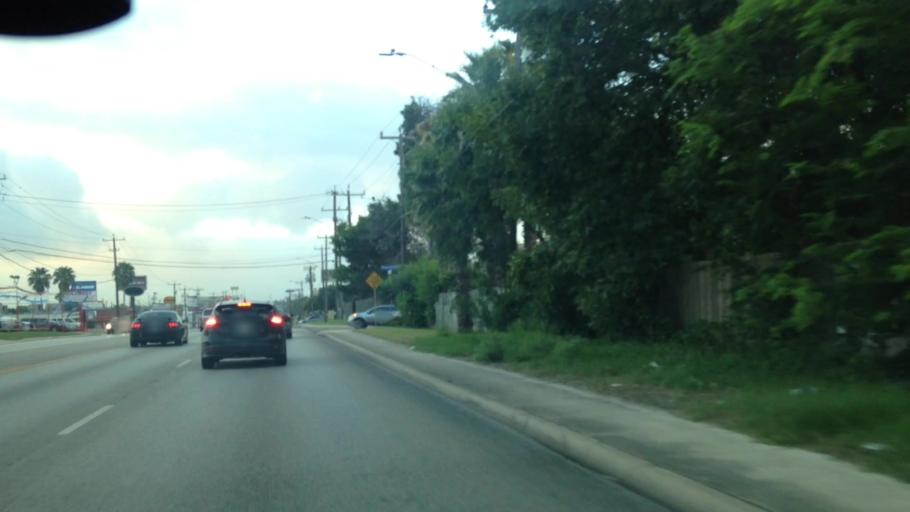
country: US
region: Texas
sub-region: Bexar County
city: Windcrest
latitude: 29.5280
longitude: -98.4111
